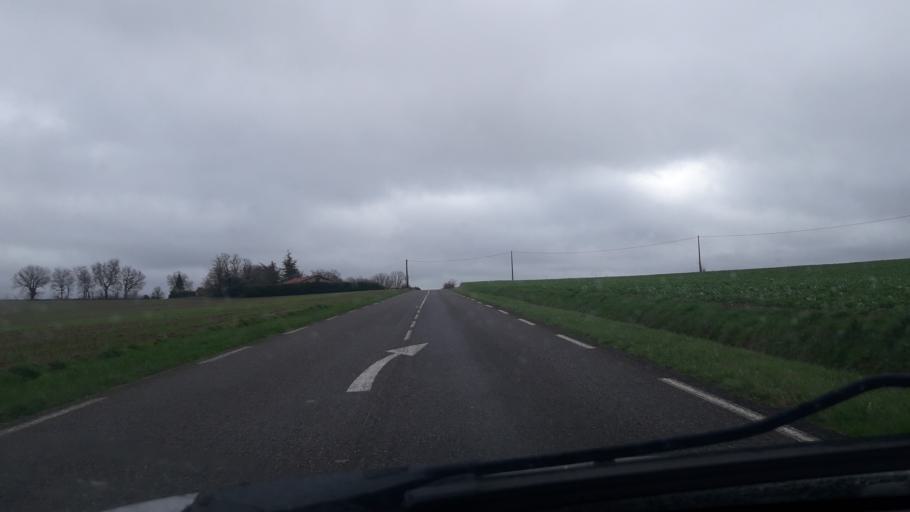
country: FR
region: Midi-Pyrenees
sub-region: Departement du Gers
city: Gimont
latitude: 43.7056
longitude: 0.9927
